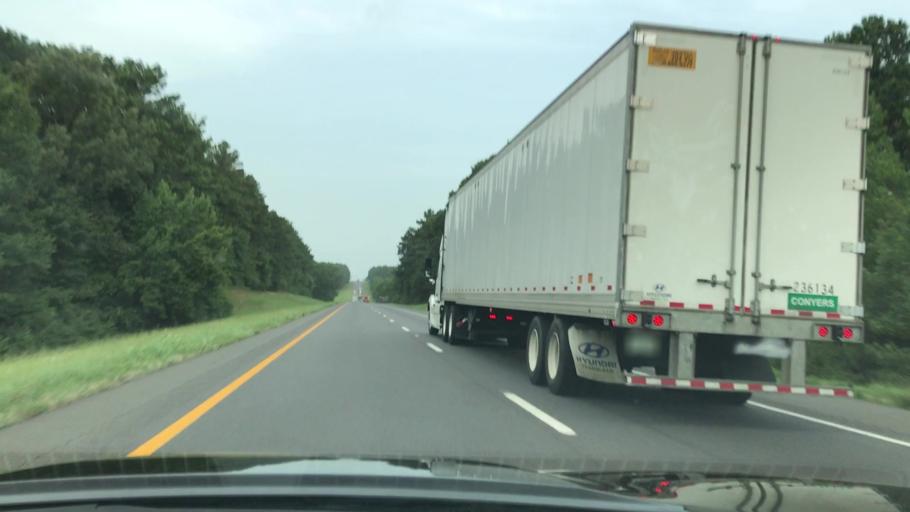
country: US
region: Texas
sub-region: Harrison County
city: Marshall
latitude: 32.4898
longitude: -94.3923
